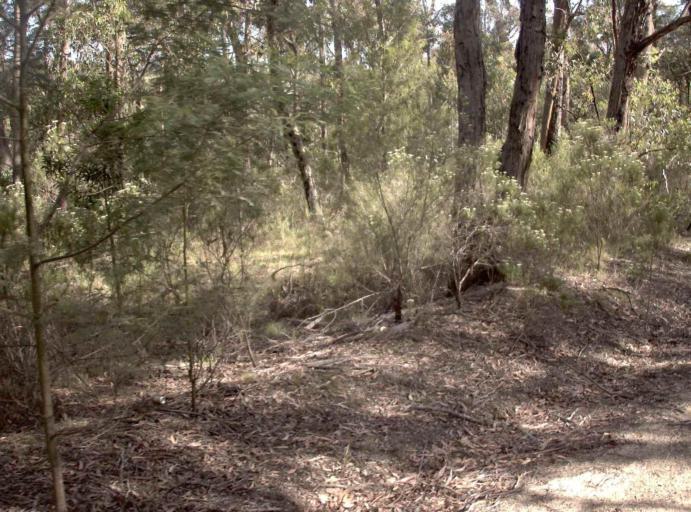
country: AU
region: Victoria
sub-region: East Gippsland
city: Lakes Entrance
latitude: -37.5510
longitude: 148.1471
